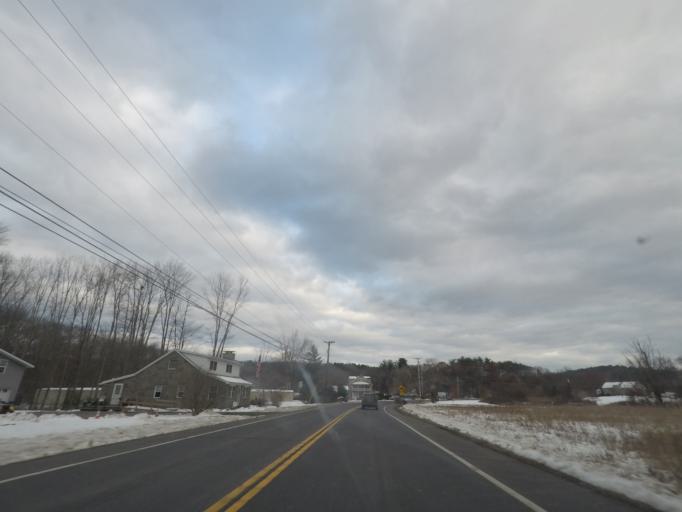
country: US
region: New York
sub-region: Ulster County
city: Tillson
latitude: 41.8198
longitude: -74.0605
